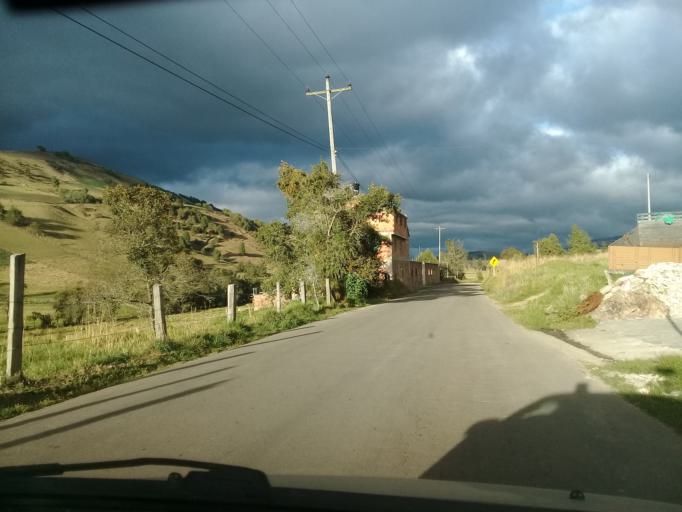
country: CO
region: Cundinamarca
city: Villapinzon
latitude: 5.2201
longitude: -73.6174
